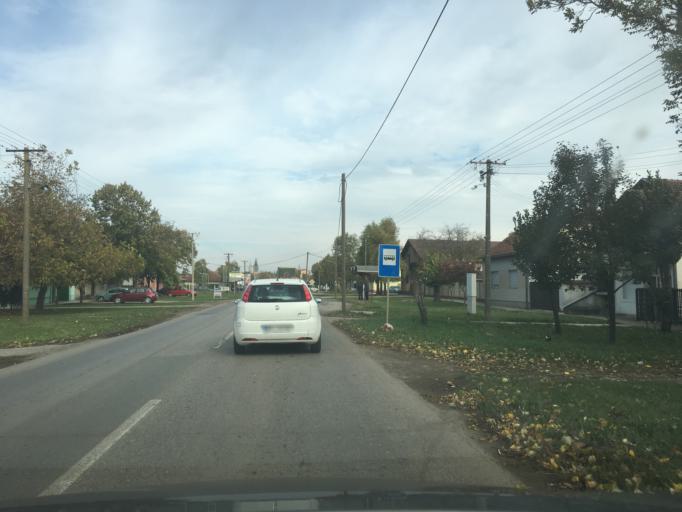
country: RS
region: Autonomna Pokrajina Vojvodina
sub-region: Juznobacki Okrug
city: Zabalj
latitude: 45.3622
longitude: 20.0654
